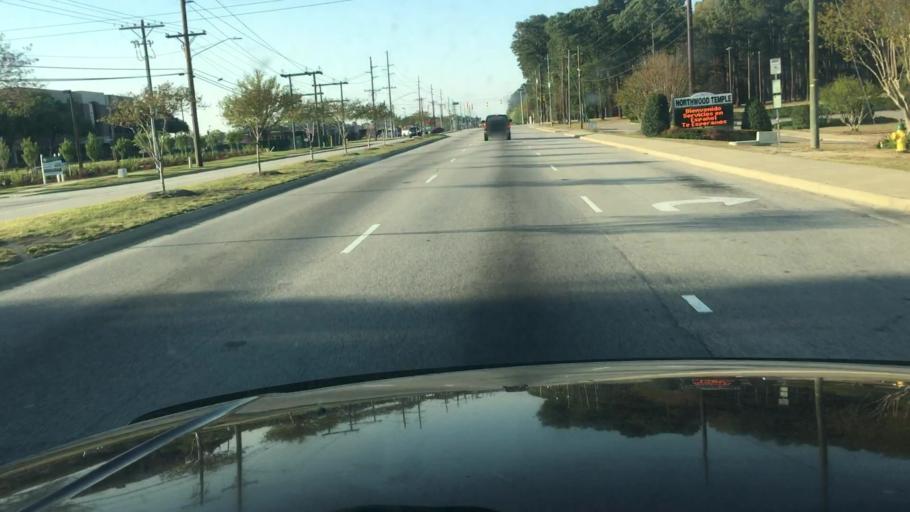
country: US
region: North Carolina
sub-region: Cumberland County
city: Fayetteville
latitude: 35.1183
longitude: -78.8798
